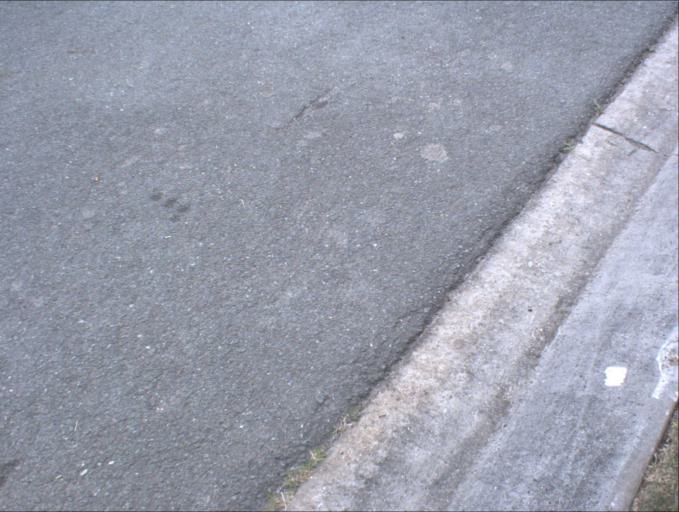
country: AU
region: Queensland
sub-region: Logan
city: Beenleigh
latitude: -27.7216
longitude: 153.2059
